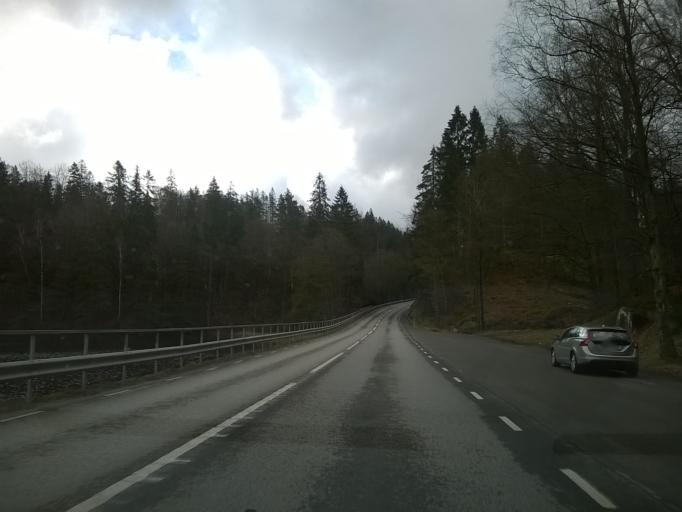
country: SE
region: Halland
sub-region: Varbergs Kommun
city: Tvaaker
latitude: 57.1521
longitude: 12.5908
